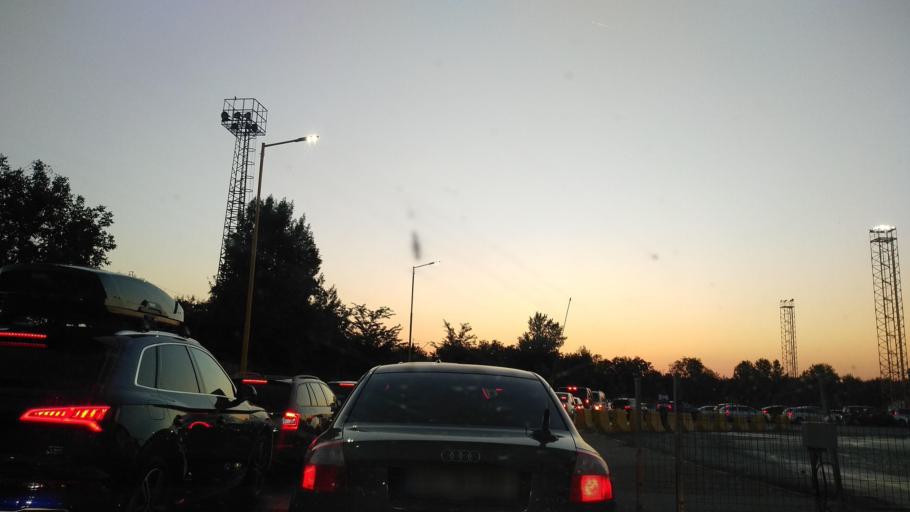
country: RO
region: Giurgiu
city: Giurgiu
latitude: 43.8804
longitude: 26.0150
